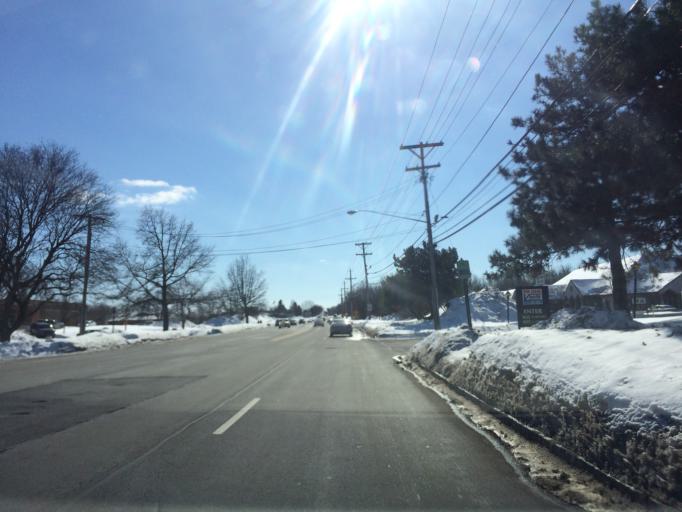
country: US
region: New York
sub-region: Monroe County
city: Rochester
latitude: 43.1249
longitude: -77.5933
